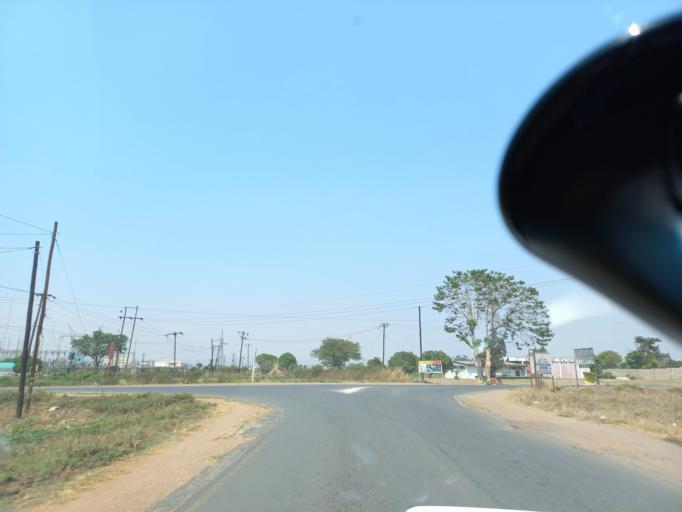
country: ZM
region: Lusaka
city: Kafue
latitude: -15.7503
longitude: 28.1627
